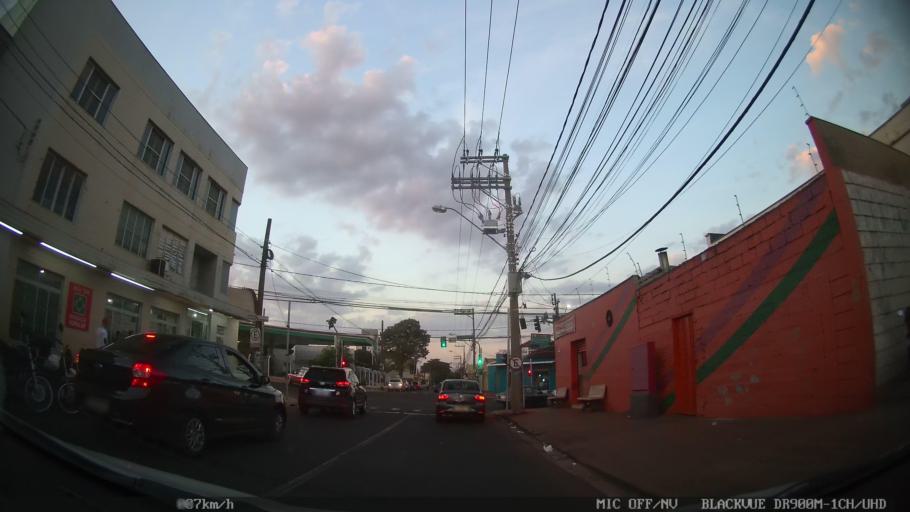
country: BR
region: Sao Paulo
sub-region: Ribeirao Preto
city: Ribeirao Preto
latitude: -21.1521
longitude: -47.8250
